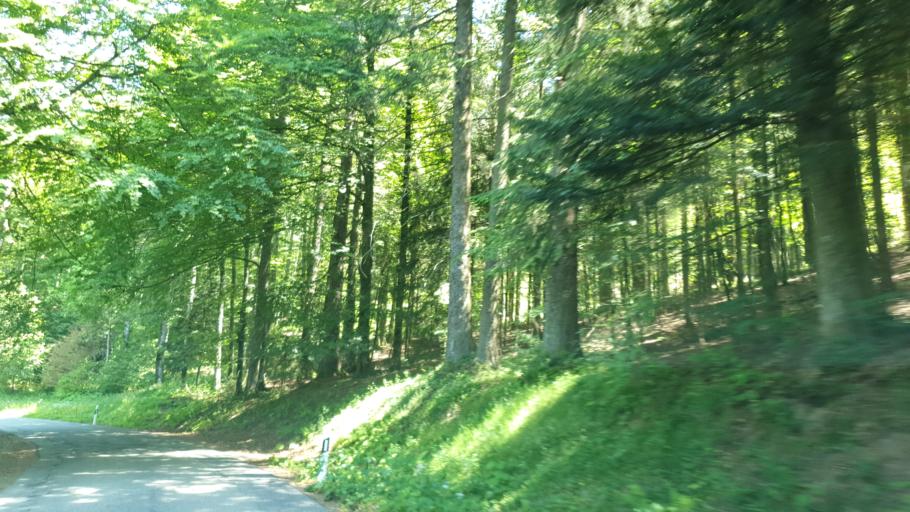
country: DE
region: Baden-Wuerttemberg
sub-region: Freiburg Region
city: Horben
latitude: 47.9030
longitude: 7.8687
